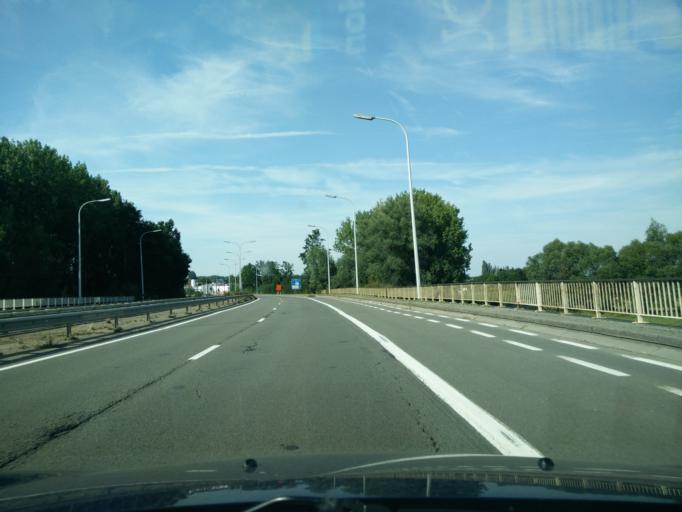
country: BE
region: Flanders
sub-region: Provincie Oost-Vlaanderen
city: Ninove
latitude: 50.8353
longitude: 4.0383
